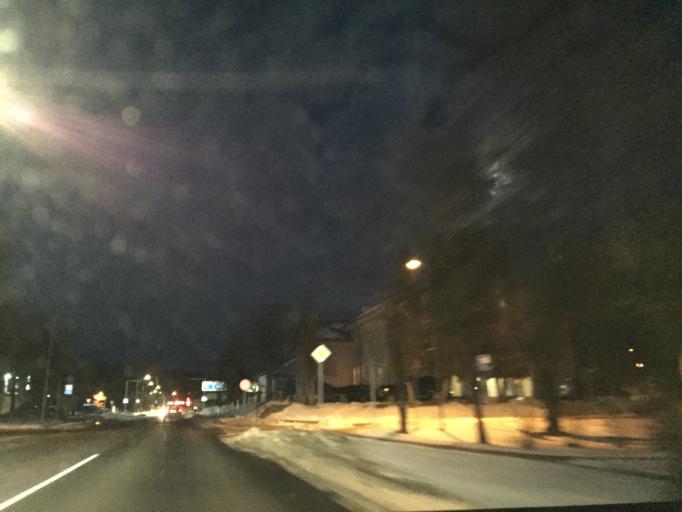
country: LV
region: Kegums
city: Kegums
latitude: 56.7427
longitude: 24.7167
